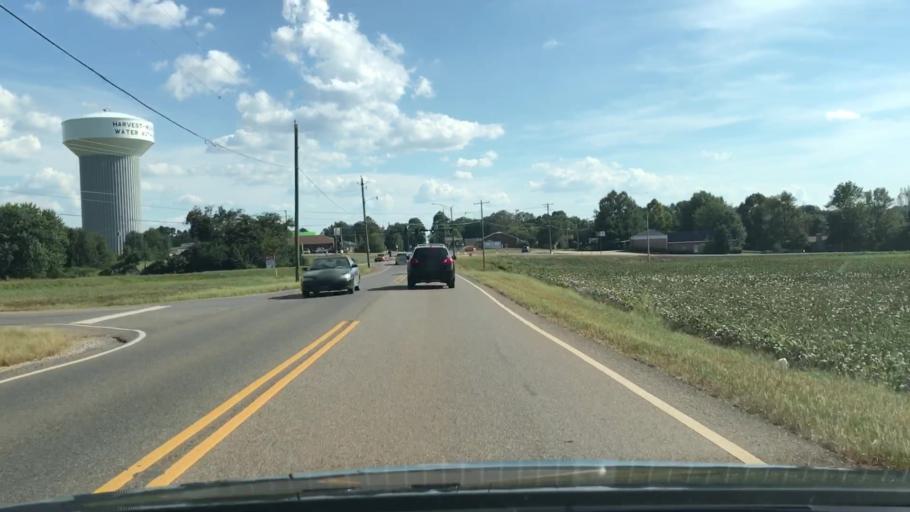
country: US
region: Alabama
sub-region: Madison County
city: Harvest
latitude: 34.8619
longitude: -86.7490
